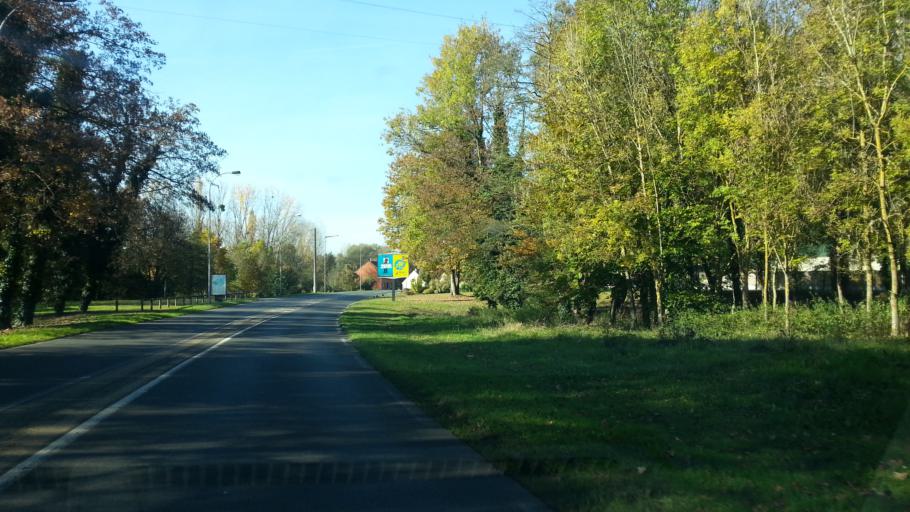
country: FR
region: Picardie
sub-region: Departement de l'Oise
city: Thiverny
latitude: 49.2553
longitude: 2.4168
